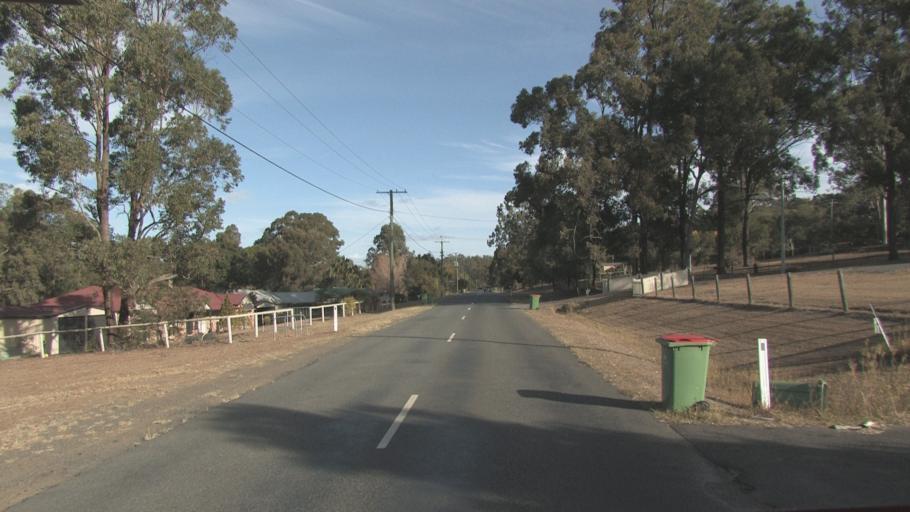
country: AU
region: Queensland
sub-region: Logan
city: Cedar Vale
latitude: -27.8753
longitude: 153.0108
